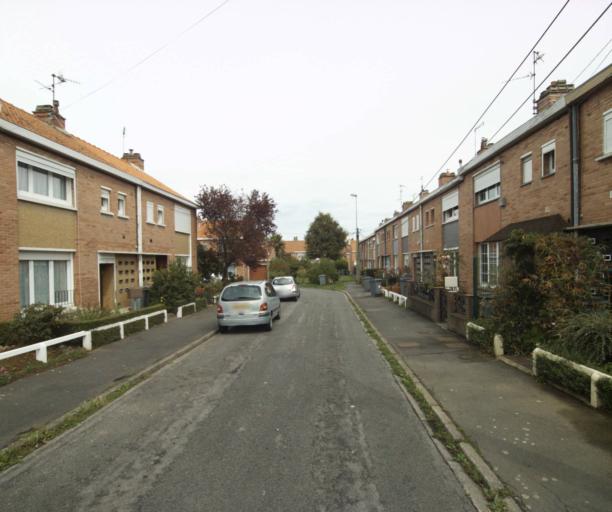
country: FR
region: Nord-Pas-de-Calais
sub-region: Departement du Nord
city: Faches-Thumesnil
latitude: 50.5952
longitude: 3.0752
